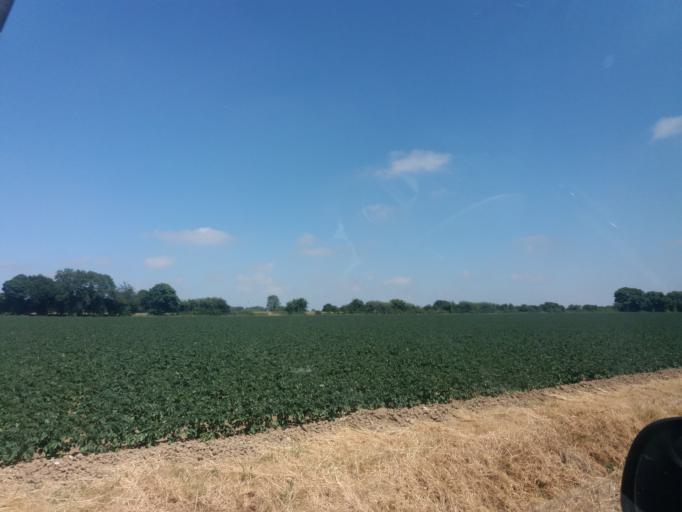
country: IE
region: Leinster
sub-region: Fingal County
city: Swords
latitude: 53.5195
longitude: -6.2625
